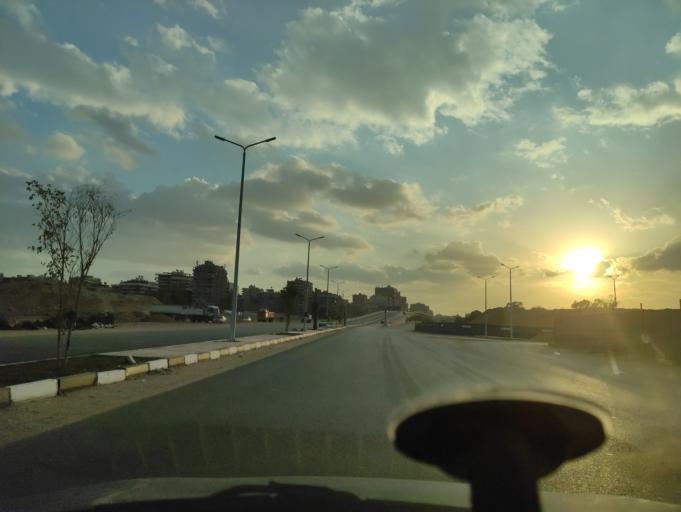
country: EG
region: Muhafazat al Qalyubiyah
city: Al Khankah
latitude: 30.1225
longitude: 31.3547
